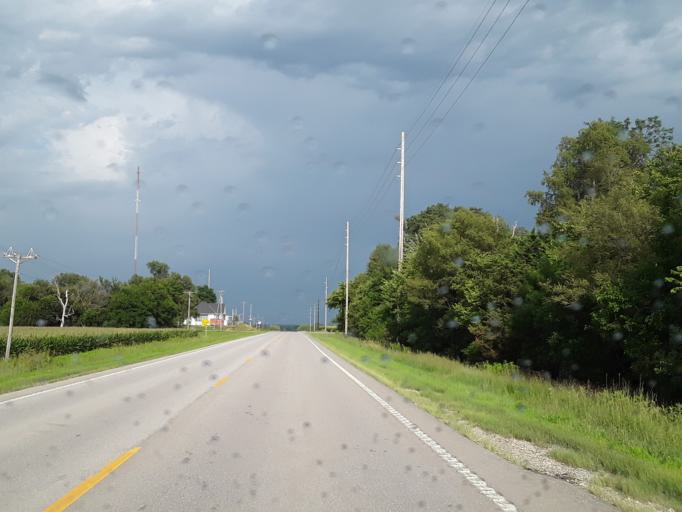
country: US
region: Nebraska
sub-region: Saunders County
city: Ashland
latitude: 41.0887
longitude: -96.3902
